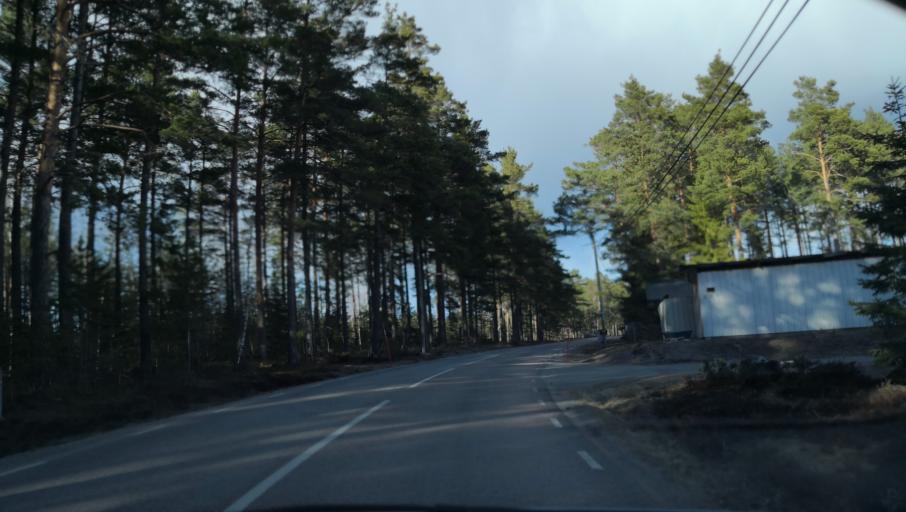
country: SE
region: Stockholm
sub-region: Varmdo Kommun
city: Mortnas
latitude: 59.2741
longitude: 18.4701
